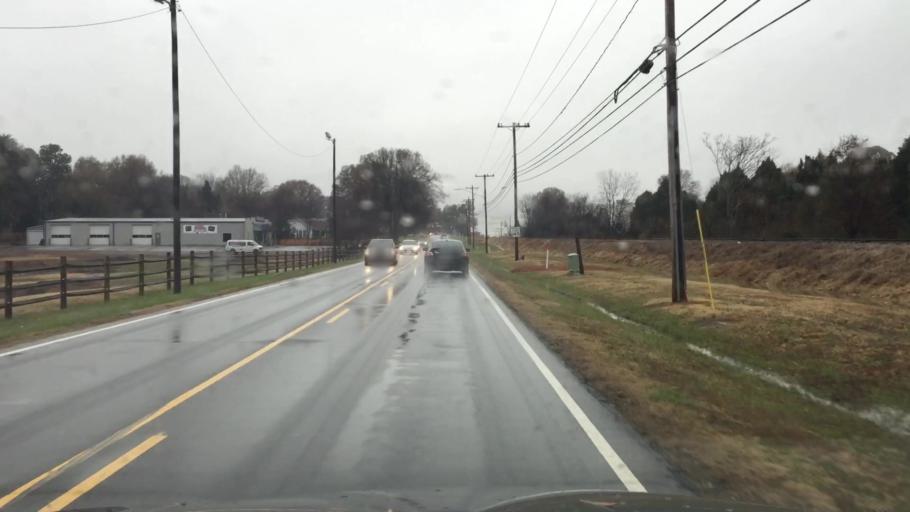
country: US
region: North Carolina
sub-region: Iredell County
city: Mooresville
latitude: 35.6085
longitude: -80.8165
